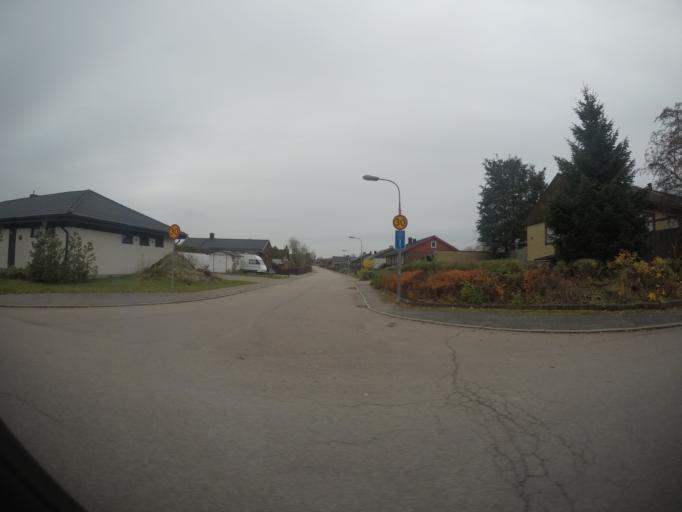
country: SE
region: Vaestmanland
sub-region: Vasteras
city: Vasteras
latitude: 59.6310
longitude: 16.4921
